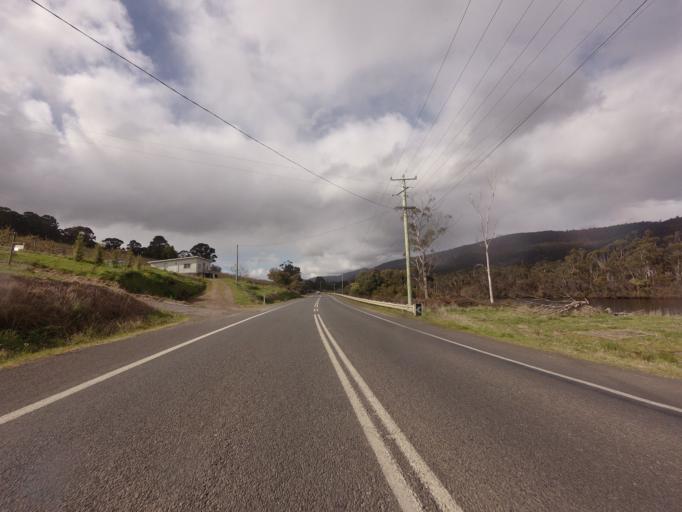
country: AU
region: Tasmania
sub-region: Huon Valley
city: Huonville
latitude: -43.0569
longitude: 147.0309
